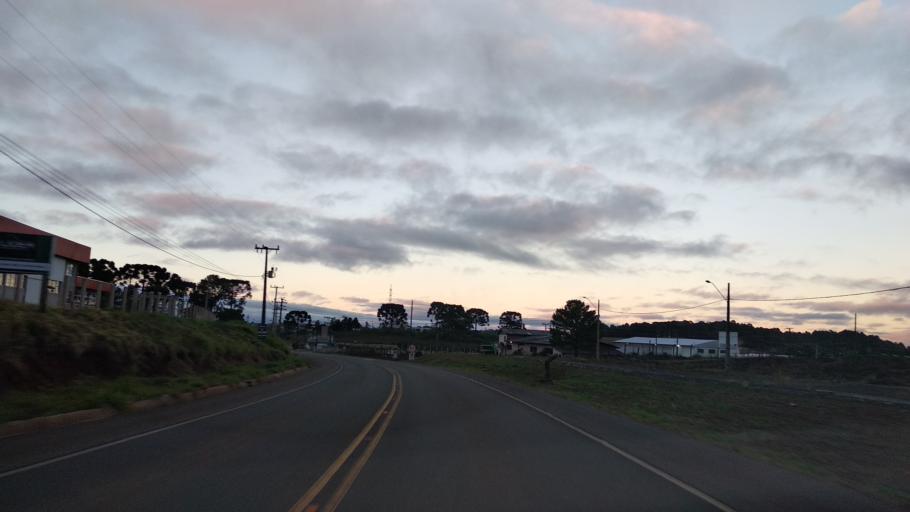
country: BR
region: Santa Catarina
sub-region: Campos Novos
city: Campos Novos
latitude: -27.3788
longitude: -51.2084
